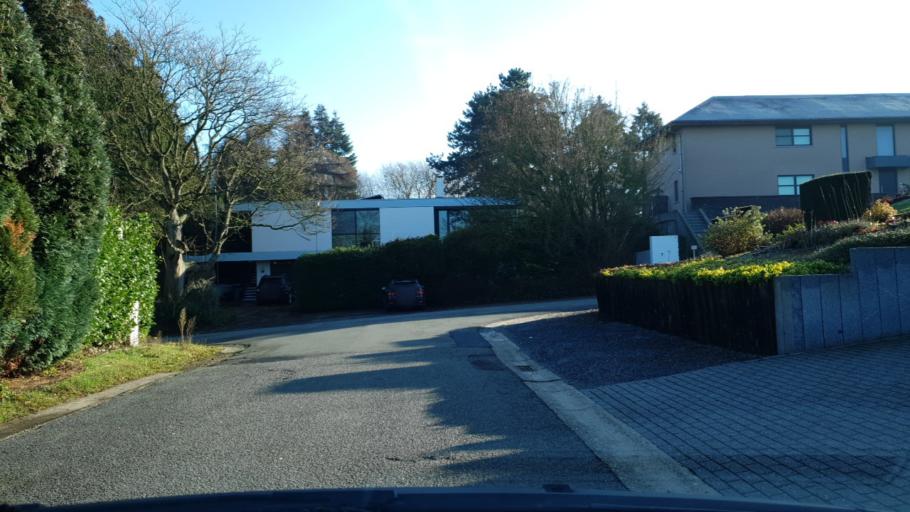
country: BE
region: Flanders
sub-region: Provincie Vlaams-Brabant
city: Herent
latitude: 50.8877
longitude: 4.6581
